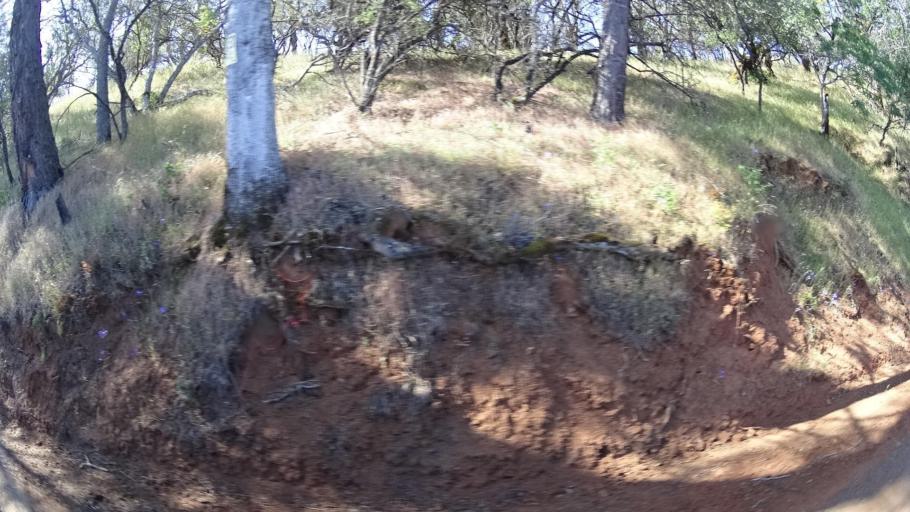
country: US
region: California
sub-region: Lake County
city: Clearlake Oaks
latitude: 38.9954
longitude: -122.6829
